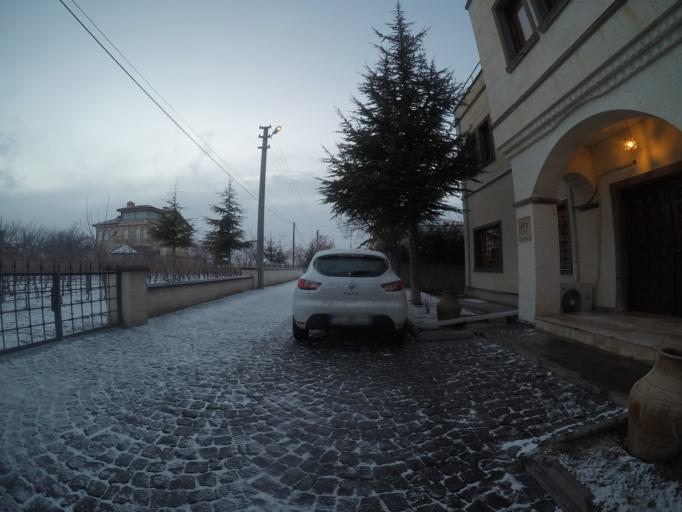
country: TR
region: Nevsehir
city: Goereme
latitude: 38.6226
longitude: 34.8041
